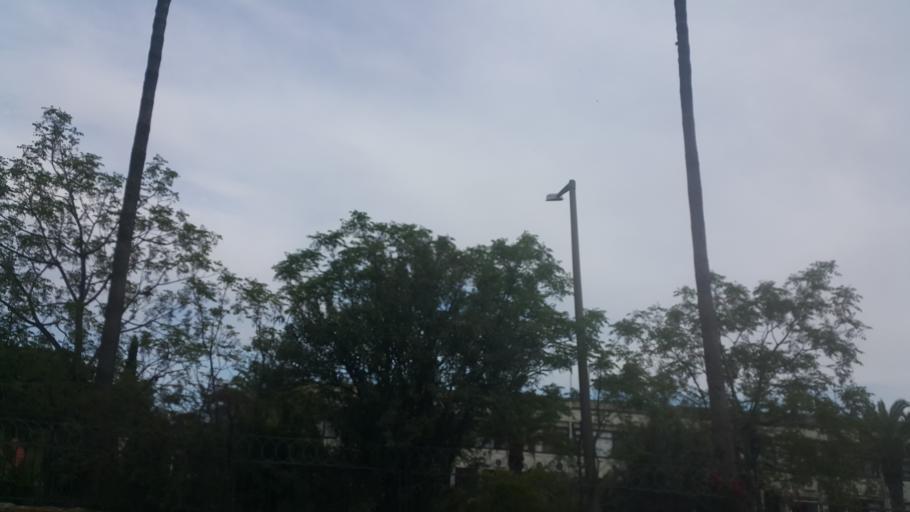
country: TR
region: Mersin
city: Tarsus
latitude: 36.9230
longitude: 34.9331
